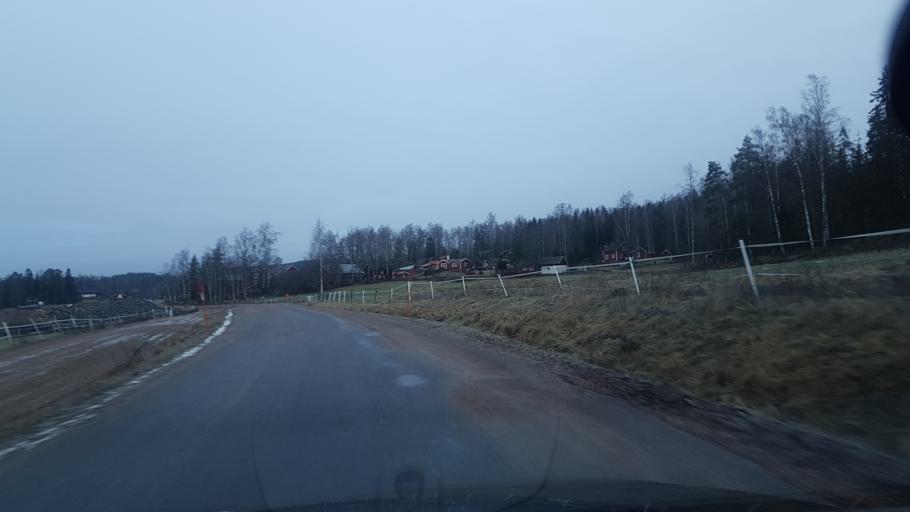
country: SE
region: Dalarna
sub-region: Borlange Kommun
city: Ornas
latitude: 60.4418
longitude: 15.6455
